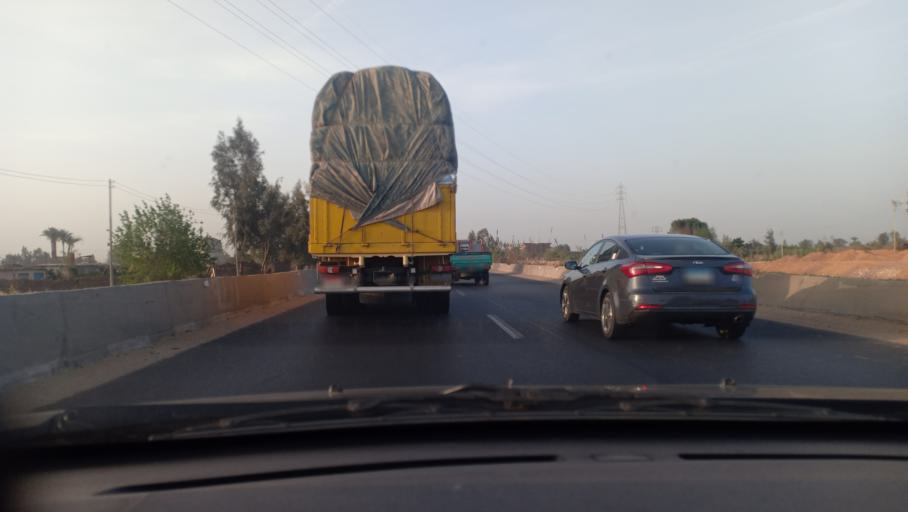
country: EG
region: Muhafazat al Minufiyah
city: Quwaysina
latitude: 30.5665
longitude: 31.2708
